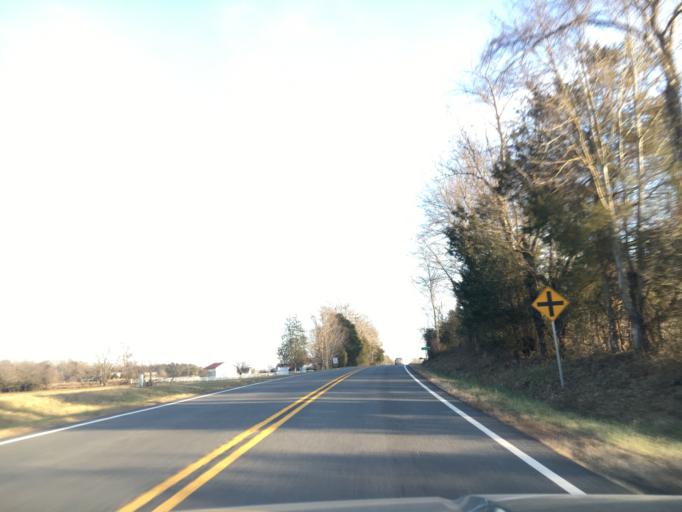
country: US
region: Virginia
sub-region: Culpeper County
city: Merrimac
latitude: 38.5511
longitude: -78.1391
